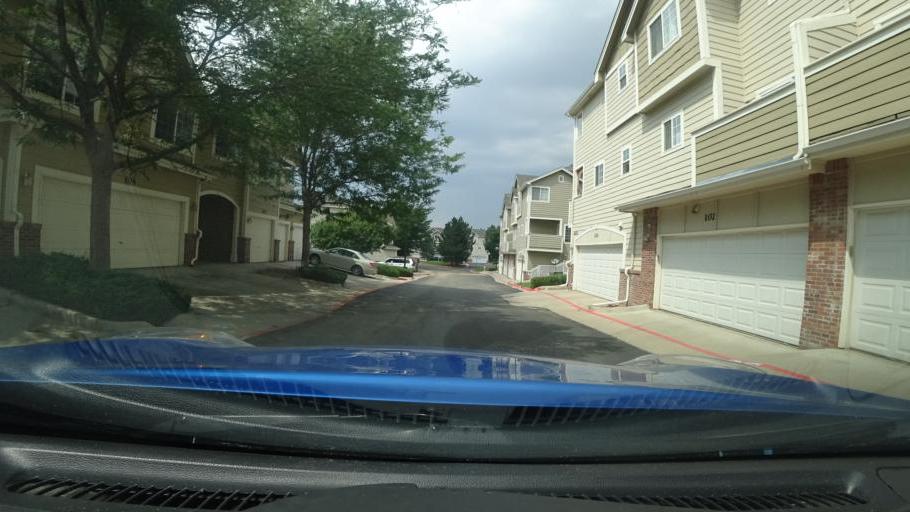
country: US
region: Colorado
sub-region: Adams County
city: Aurora
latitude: 39.6872
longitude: -104.7634
